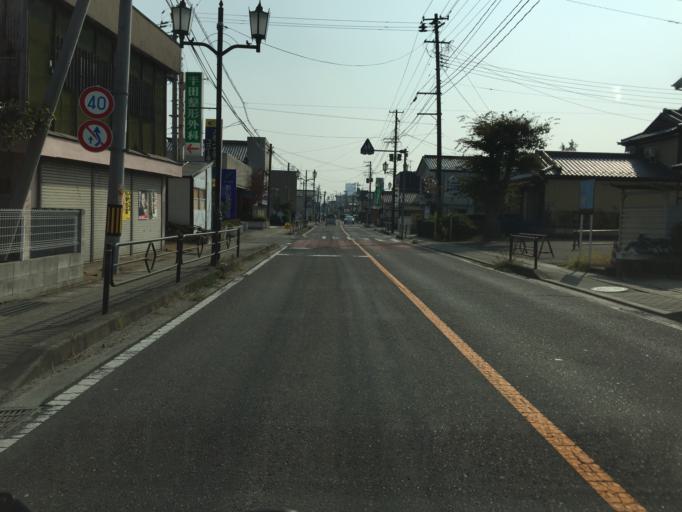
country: JP
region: Fukushima
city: Koriyama
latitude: 37.4221
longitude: 140.3916
